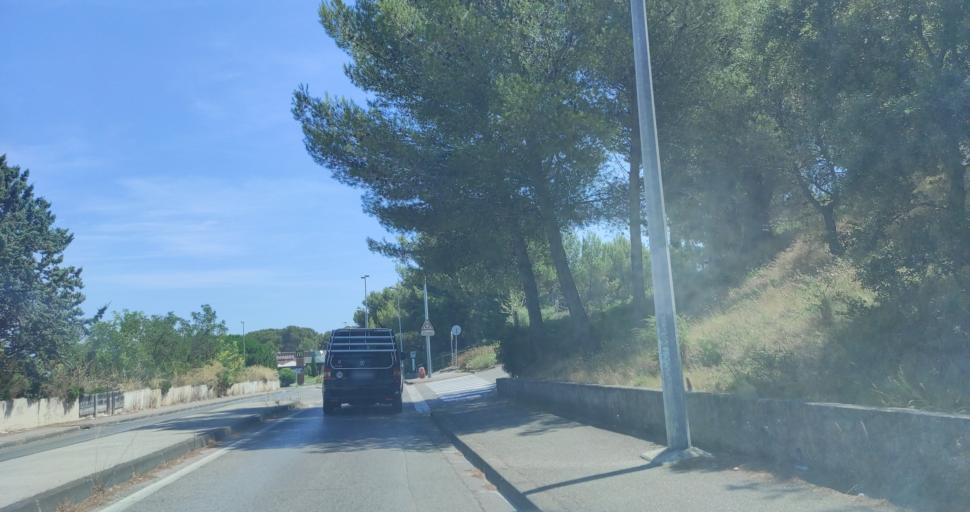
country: FR
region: Provence-Alpes-Cote d'Azur
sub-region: Departement des Bouches-du-Rhone
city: Martigues
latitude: 43.4218
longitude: 5.0523
